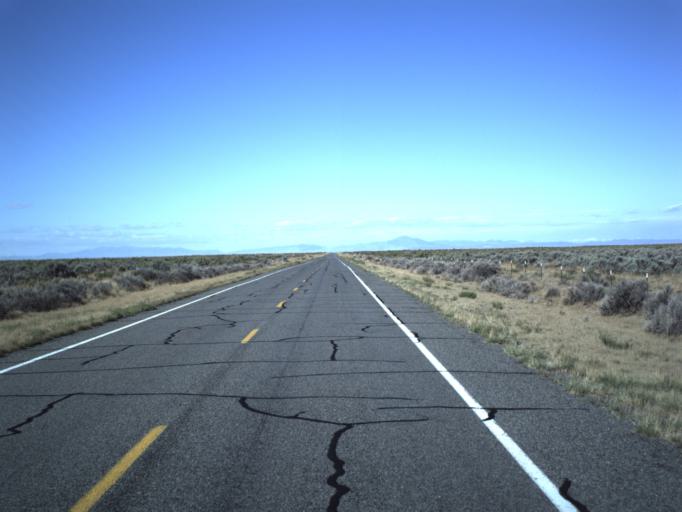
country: US
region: Utah
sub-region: Millard County
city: Delta
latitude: 39.3538
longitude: -112.4508
